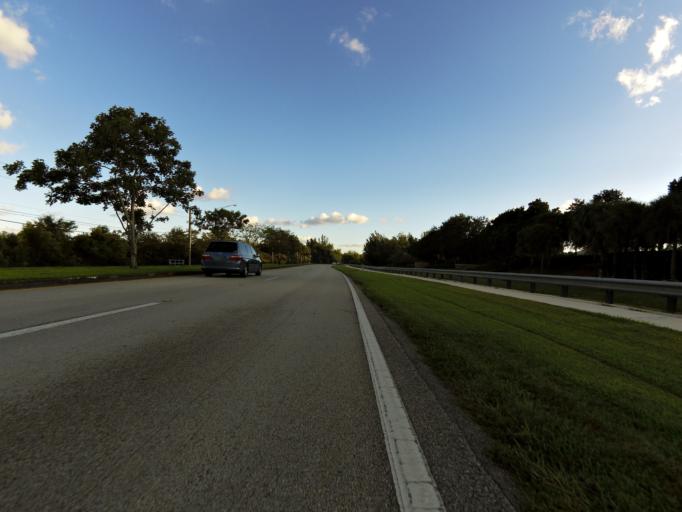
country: US
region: Florida
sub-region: Broward County
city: Cooper City
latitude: 26.0740
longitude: -80.2809
